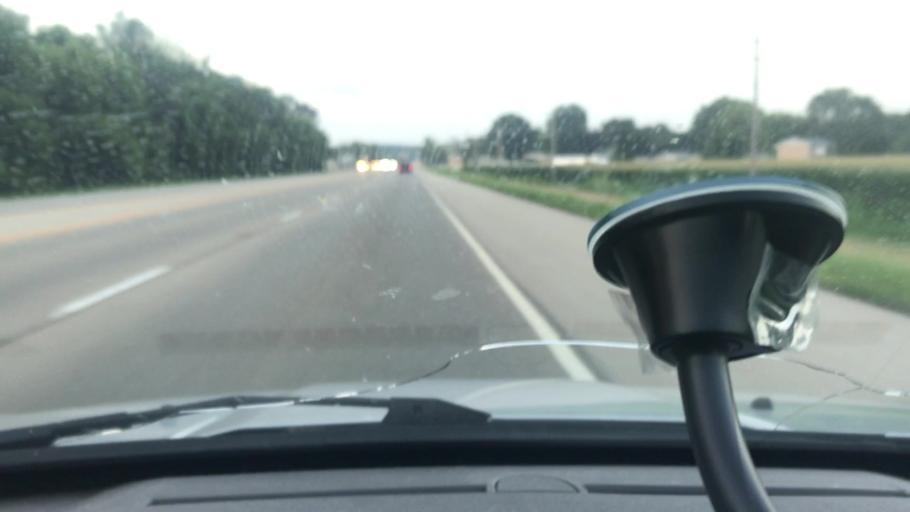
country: US
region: Illinois
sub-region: Tazewell County
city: North Pekin
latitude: 40.6152
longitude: -89.6295
